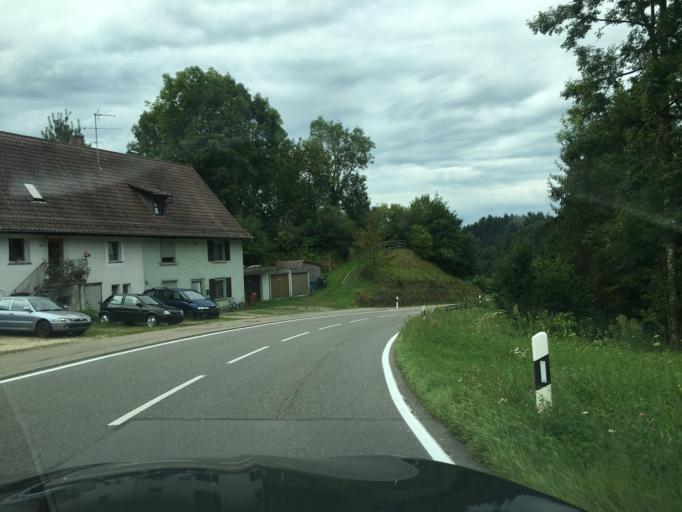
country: DE
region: Baden-Wuerttemberg
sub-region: Tuebingen Region
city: Rot
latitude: 47.8696
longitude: 9.1098
